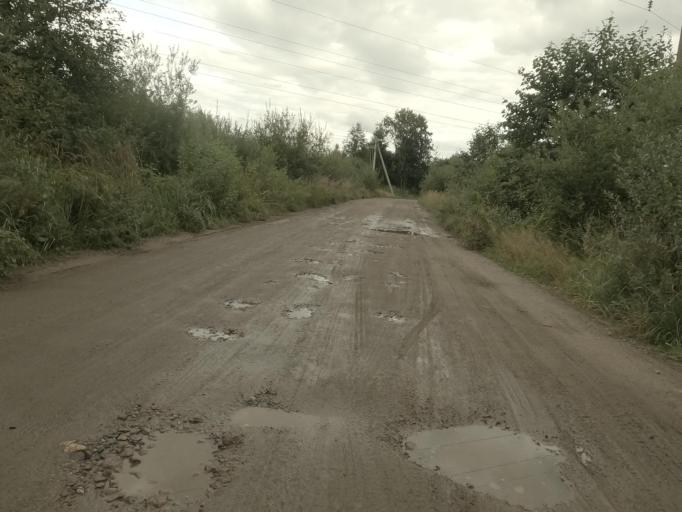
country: RU
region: Leningrad
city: Kirovsk
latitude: 59.8912
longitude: 31.0027
